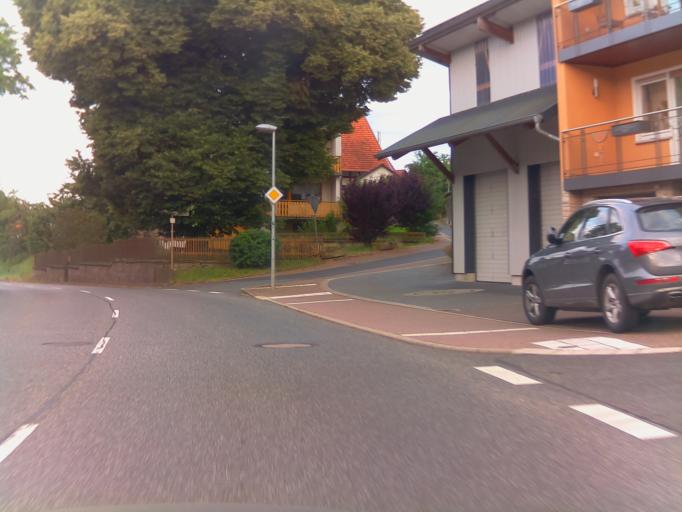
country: DE
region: Hesse
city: Grebenau
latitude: 50.7793
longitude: 9.4777
